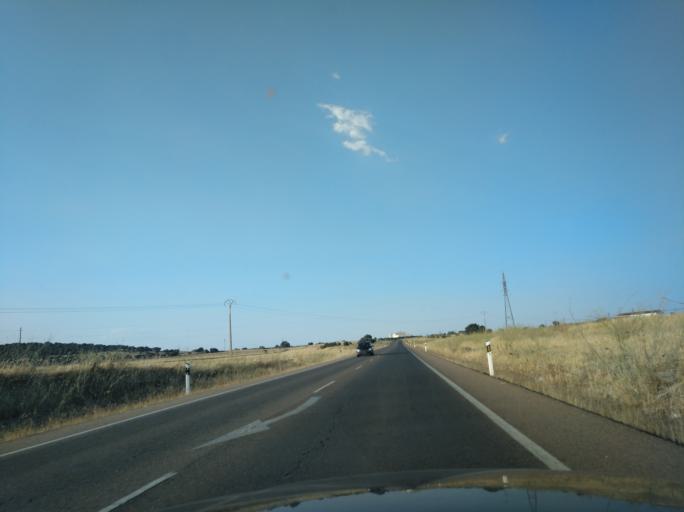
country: ES
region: Extremadura
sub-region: Provincia de Badajoz
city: Olivenza
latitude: 38.7002
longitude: -7.0888
